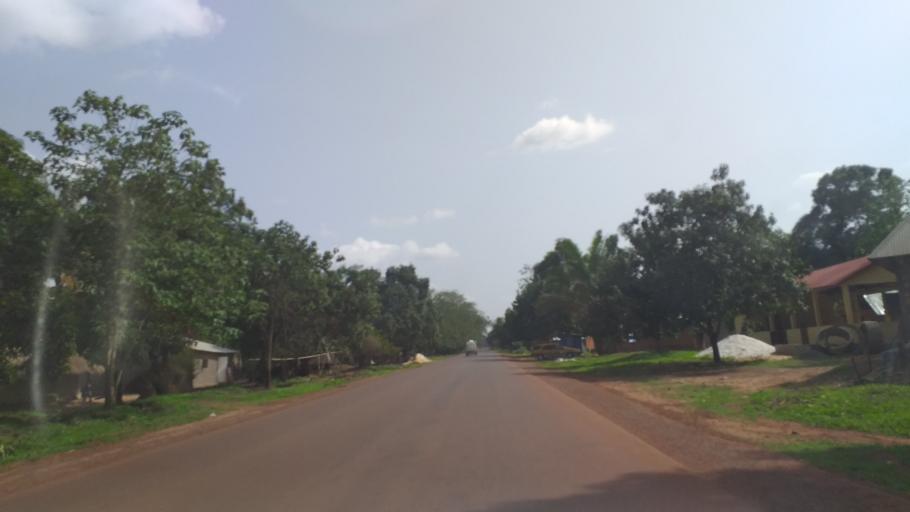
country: GN
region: Boke
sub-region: Boke Prefecture
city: Sangueya
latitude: 10.8207
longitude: -14.3747
